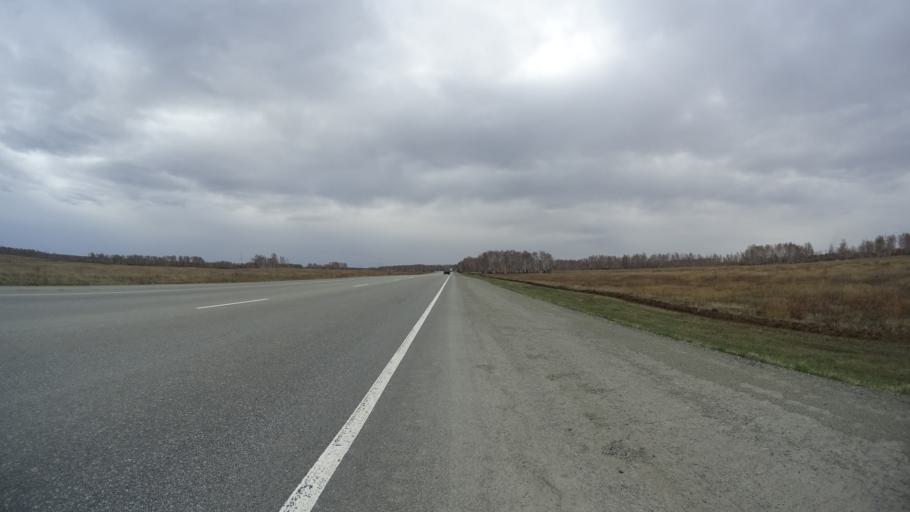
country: RU
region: Chelyabinsk
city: Yemanzhelinsk
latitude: 54.7023
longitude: 61.2538
